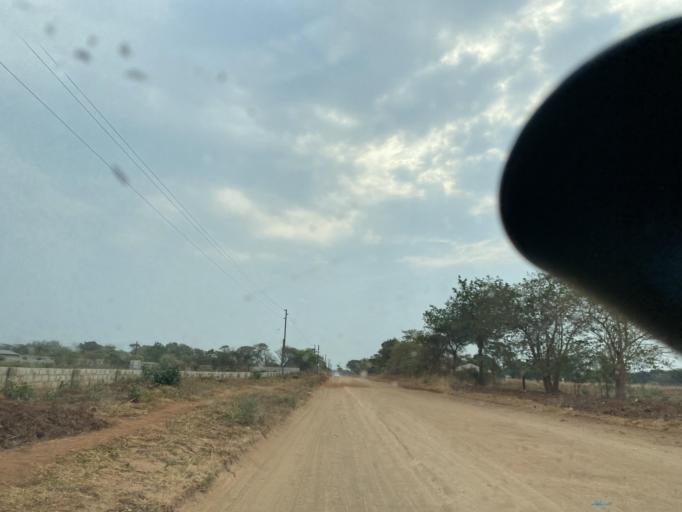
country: ZM
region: Lusaka
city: Lusaka
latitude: -15.2894
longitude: 28.2819
